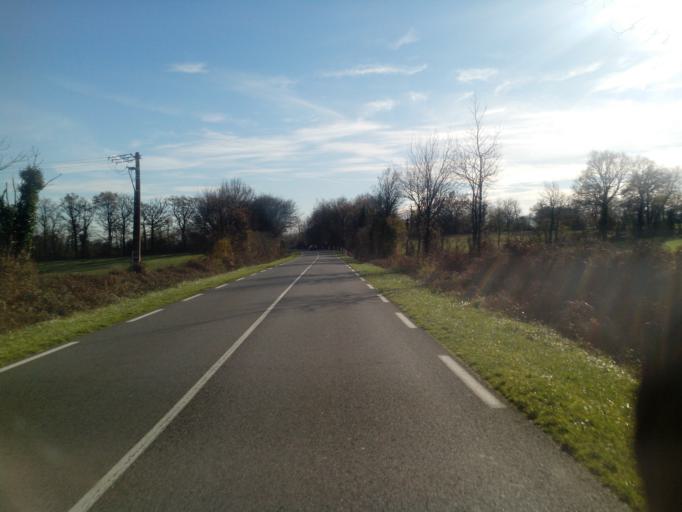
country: FR
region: Limousin
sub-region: Departement de la Haute-Vienne
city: Bussiere-Poitevine
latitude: 46.1862
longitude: 0.9326
